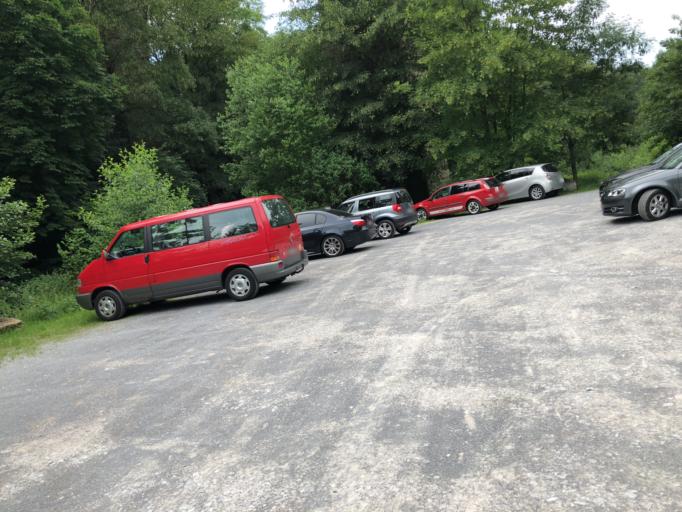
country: DE
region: North Rhine-Westphalia
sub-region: Regierungsbezirk Dusseldorf
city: Velbert
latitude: 51.3409
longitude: 7.0304
